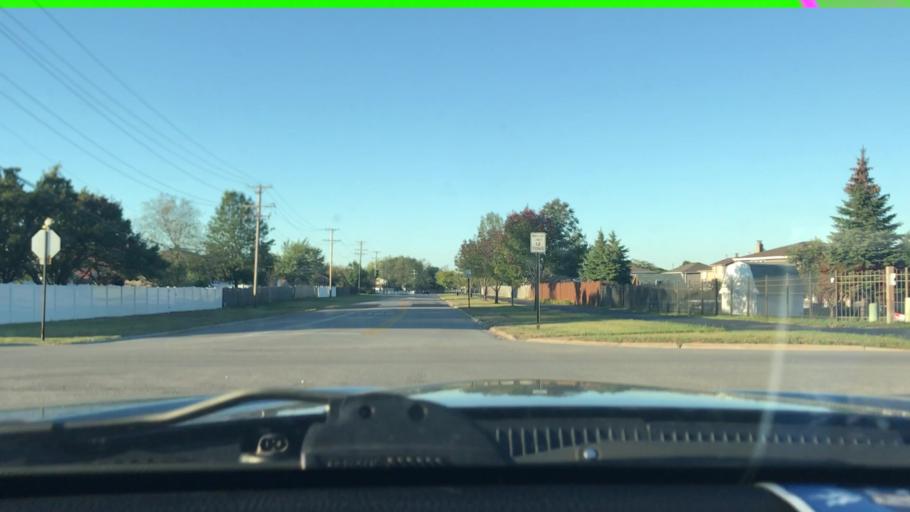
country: US
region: Illinois
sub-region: Will County
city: Frankfort Square
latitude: 41.5208
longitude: -87.8113
